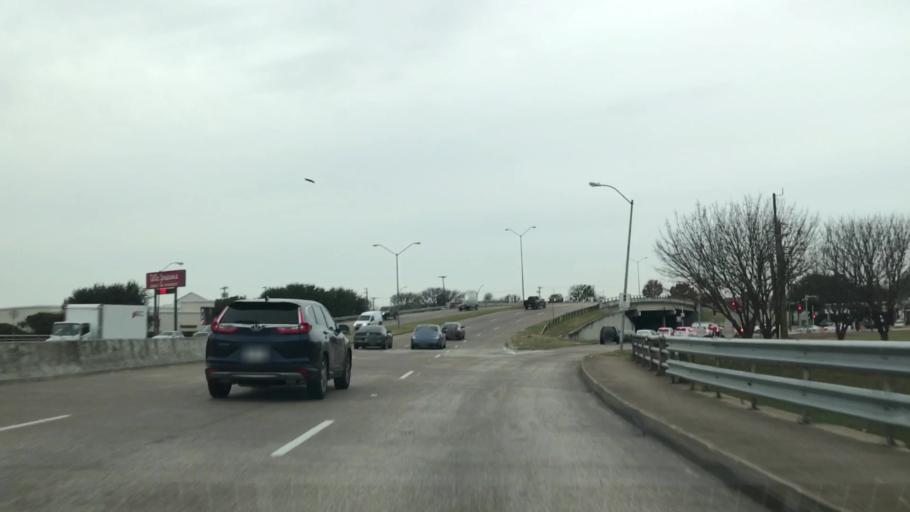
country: US
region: Texas
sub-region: Dallas County
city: University Park
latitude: 32.8599
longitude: -96.8538
